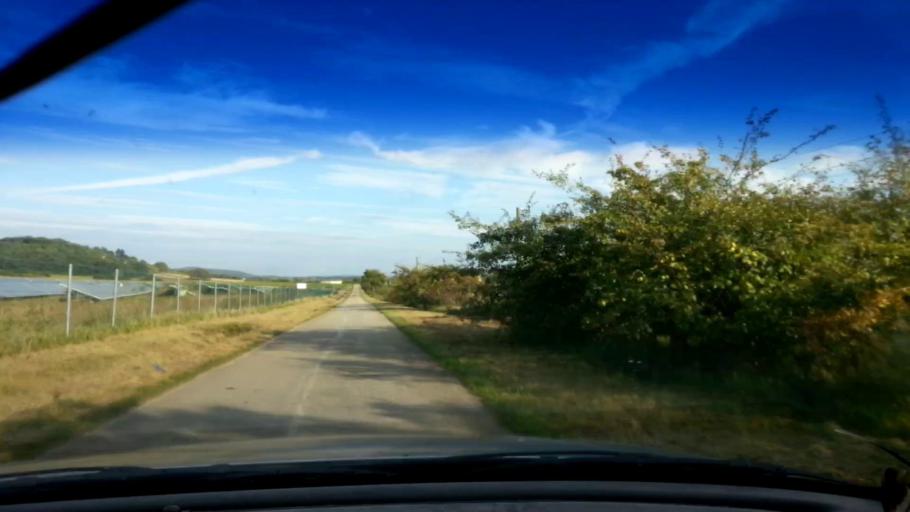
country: DE
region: Bavaria
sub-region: Upper Franconia
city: Viereth-Trunstadt
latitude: 49.9392
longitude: 10.7761
